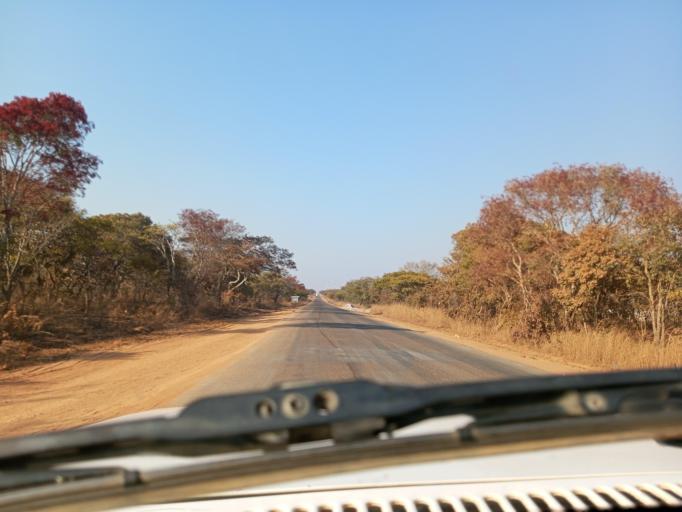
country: ZM
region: Northern
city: Mpika
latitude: -12.3981
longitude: 31.0899
